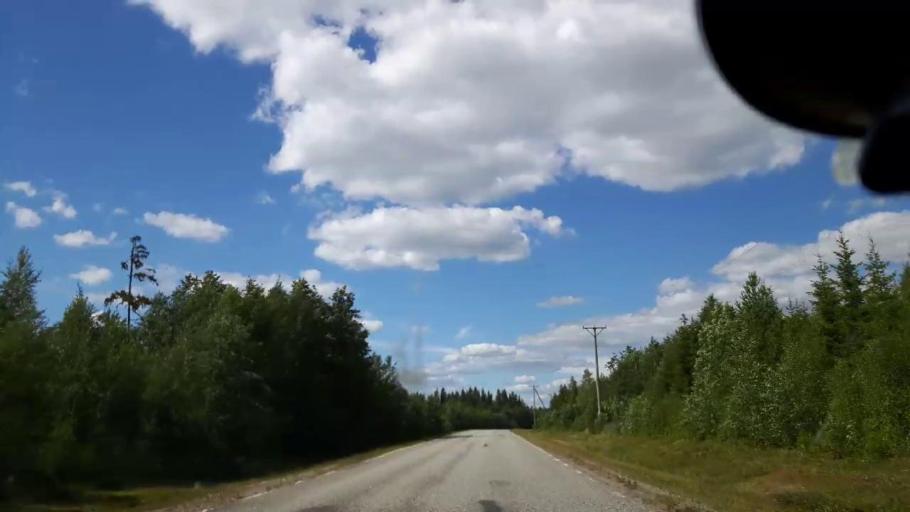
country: SE
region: Vaesternorrland
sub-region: Ange Kommun
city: Fransta
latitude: 62.7469
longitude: 16.3230
